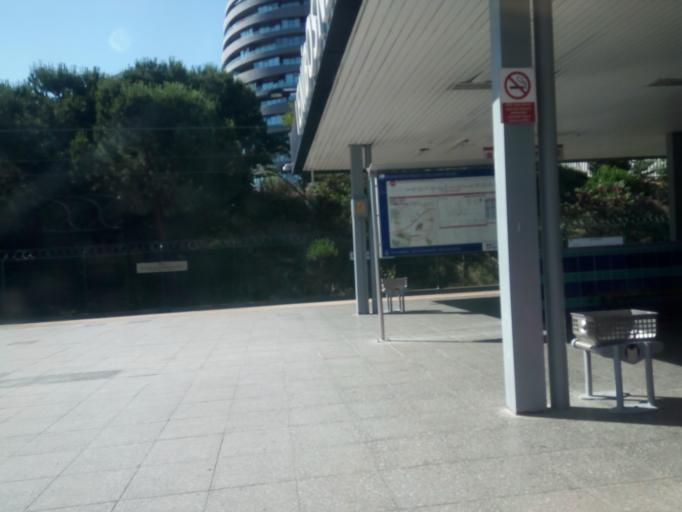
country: TR
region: Istanbul
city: Bahcelievler
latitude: 40.9892
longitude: 28.8368
